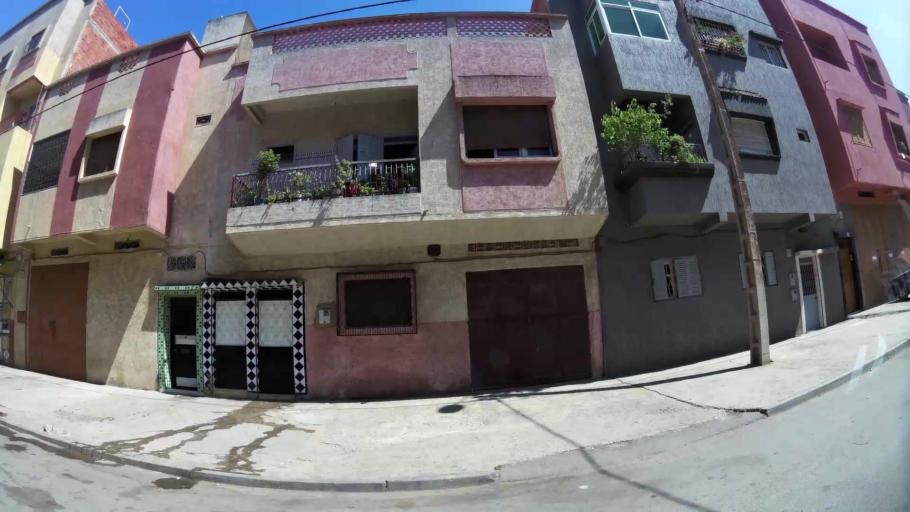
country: MA
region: Gharb-Chrarda-Beni Hssen
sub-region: Kenitra Province
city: Kenitra
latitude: 34.2448
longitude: -6.5534
